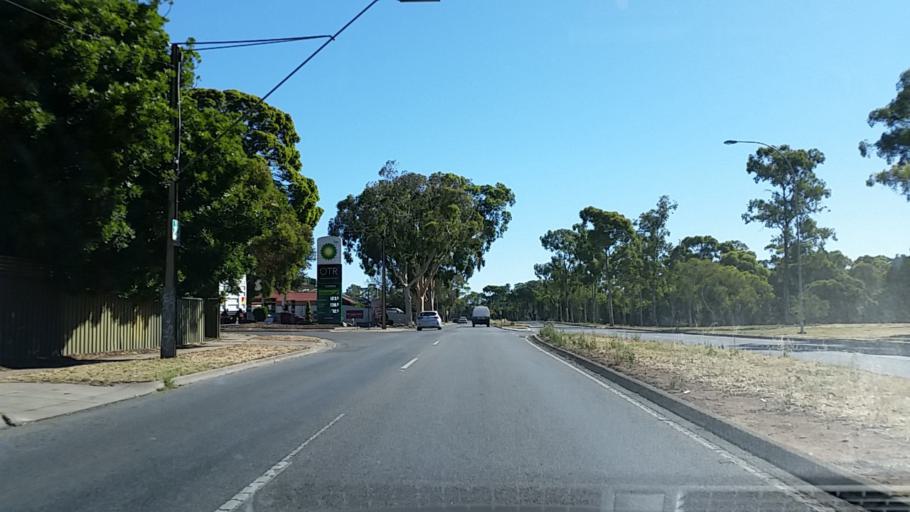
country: AU
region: South Australia
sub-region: Salisbury
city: Ingle Farm
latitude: -34.8132
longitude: 138.6435
